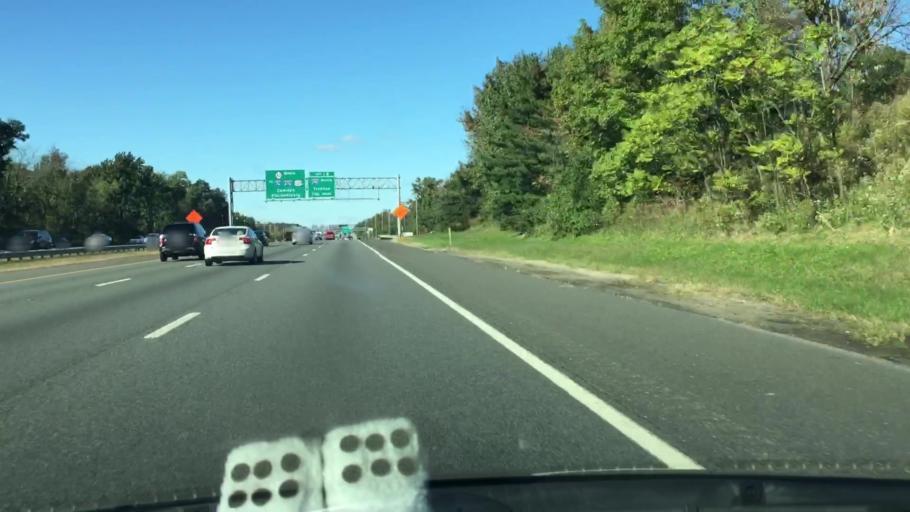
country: US
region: New Jersey
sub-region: Camden County
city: Bellmawr
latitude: 39.8465
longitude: -75.0948
